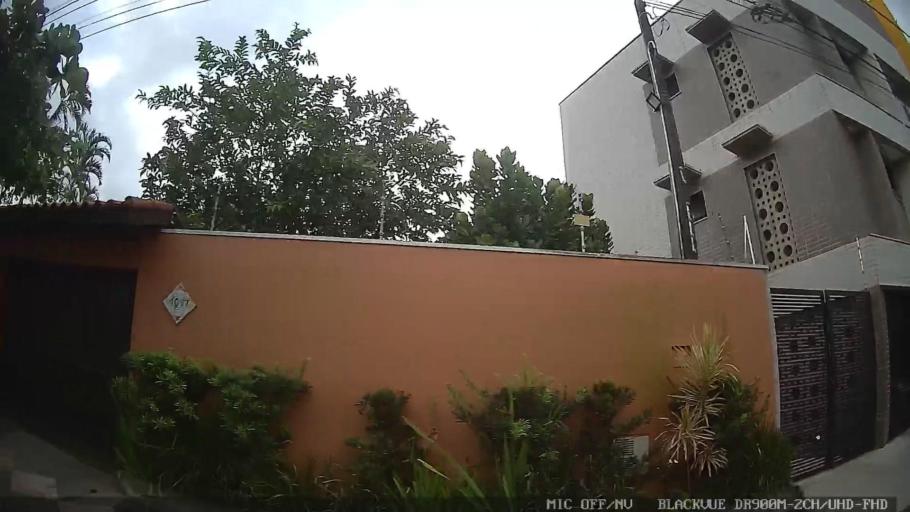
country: BR
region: Sao Paulo
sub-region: Itanhaem
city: Itanhaem
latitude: -24.1772
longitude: -46.7788
